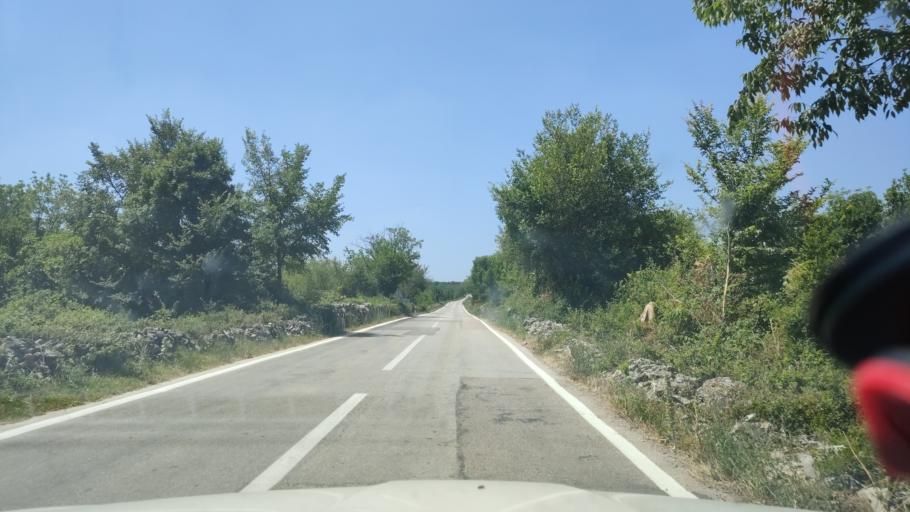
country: HR
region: Sibensko-Kniniska
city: Kistanje
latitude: 44.0133
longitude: 16.0096
